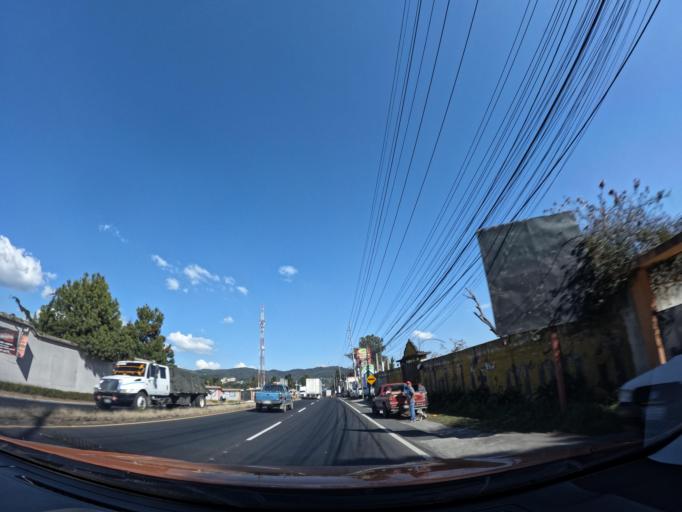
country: GT
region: Sacatepequez
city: San Bartolome Milpas Altas
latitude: 14.6079
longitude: -90.6725
